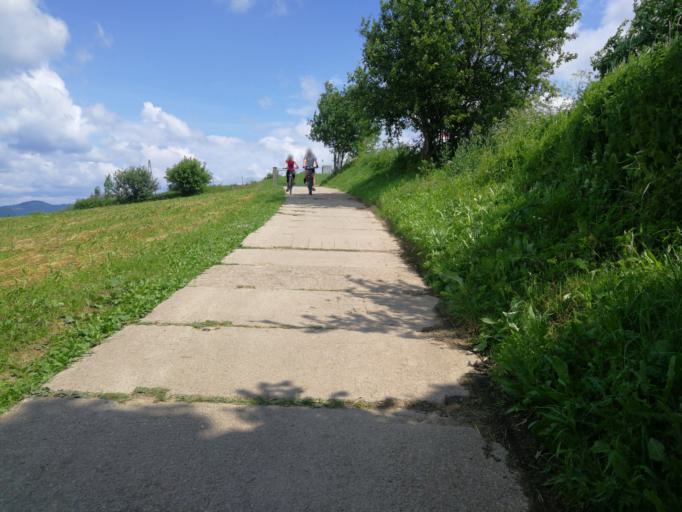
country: PL
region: Subcarpathian Voivodeship
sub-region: Powiat leski
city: Polanczyk
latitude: 49.3688
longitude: 22.4235
